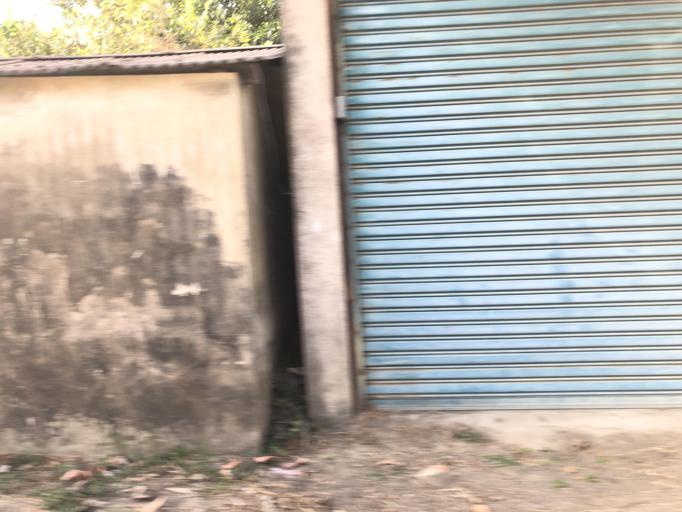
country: TW
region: Taiwan
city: Yujing
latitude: 23.0120
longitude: 120.3856
